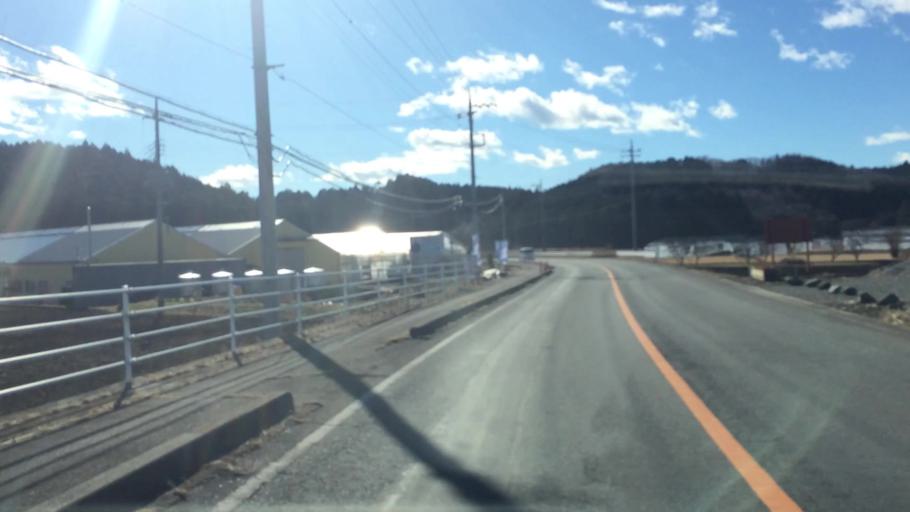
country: JP
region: Tochigi
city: Imaichi
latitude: 36.7370
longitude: 139.7477
